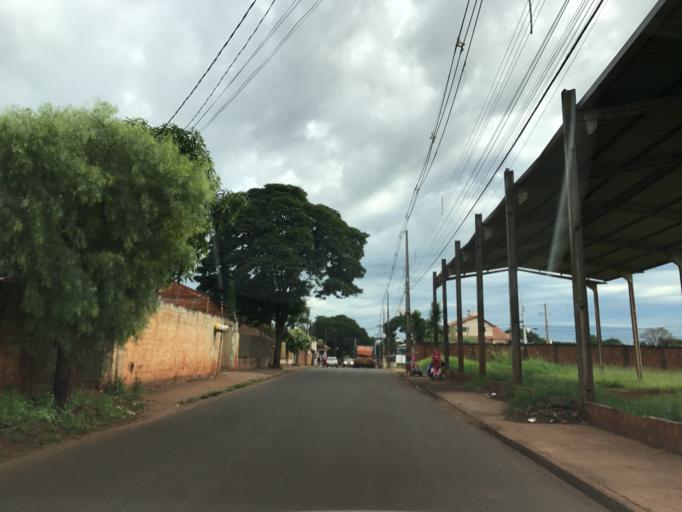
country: BR
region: Parana
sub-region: Sarandi
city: Sarandi
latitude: -23.4357
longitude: -51.8654
